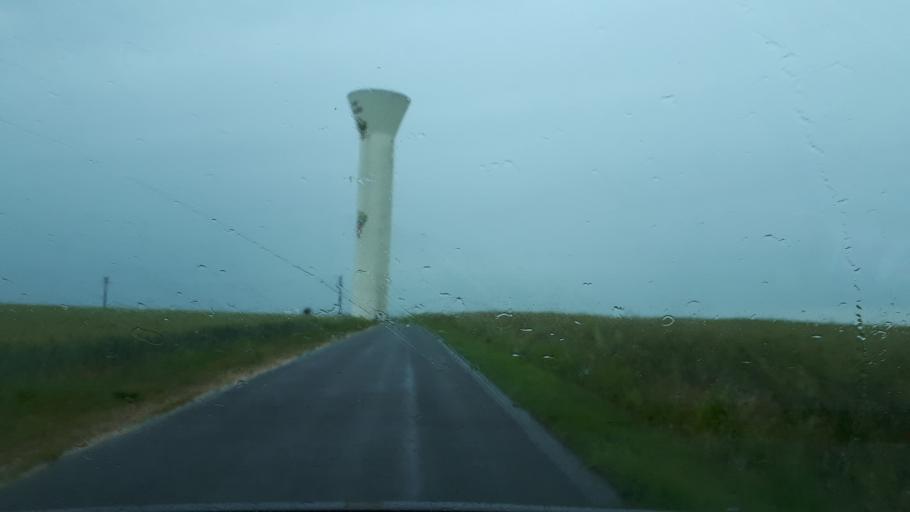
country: FR
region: Centre
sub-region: Departement du Loir-et-Cher
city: Lunay
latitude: 47.8123
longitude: 0.9264
